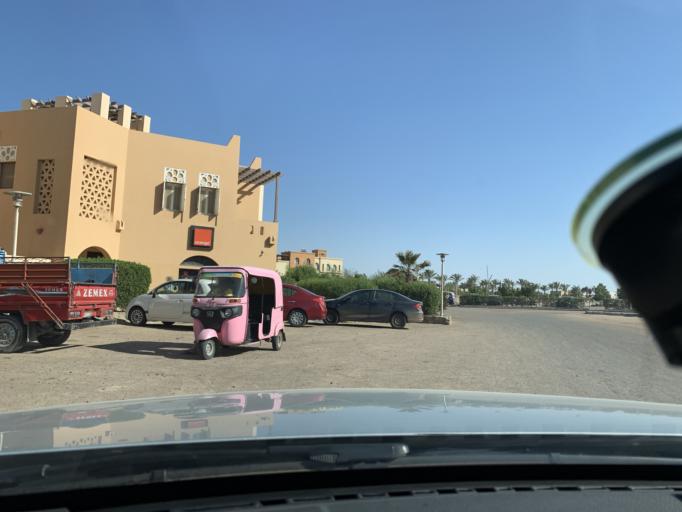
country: EG
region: Red Sea
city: El Gouna
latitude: 27.4080
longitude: 33.6734
